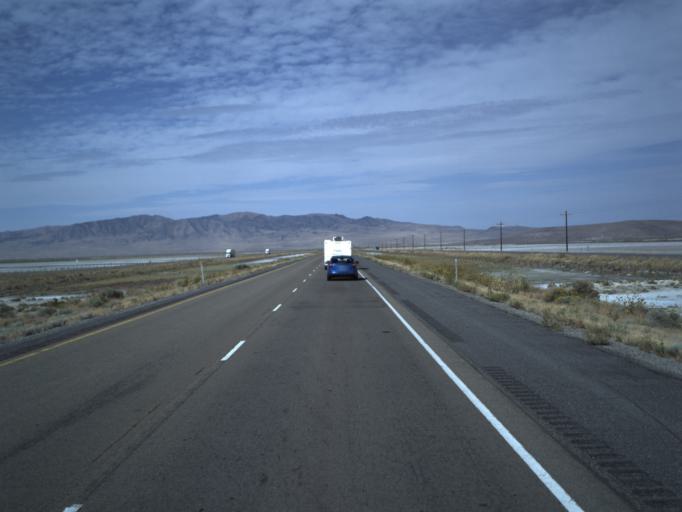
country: US
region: Utah
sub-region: Tooele County
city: Grantsville
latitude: 40.7504
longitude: -112.6959
